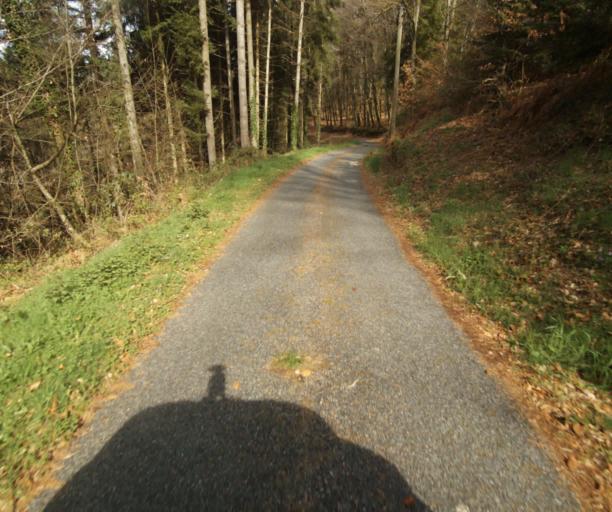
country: FR
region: Limousin
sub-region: Departement de la Correze
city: Correze
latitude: 45.3558
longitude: 1.8794
